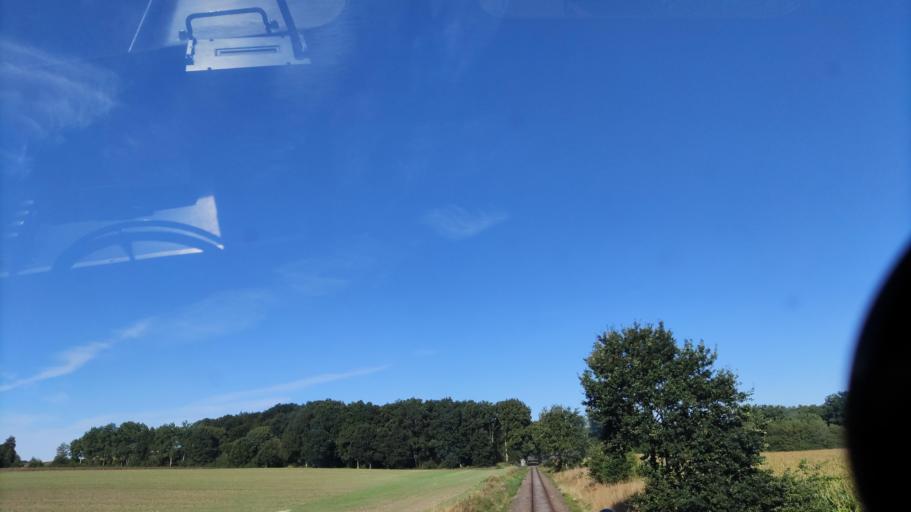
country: DE
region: Lower Saxony
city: Amelinghausen
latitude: 53.1380
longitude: 10.1930
